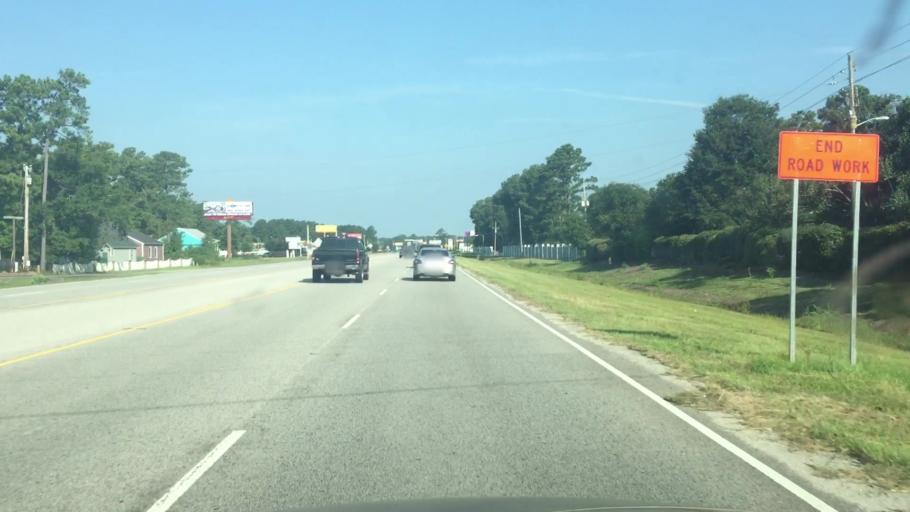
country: US
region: South Carolina
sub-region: Horry County
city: Little River
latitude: 33.8687
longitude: -78.6669
